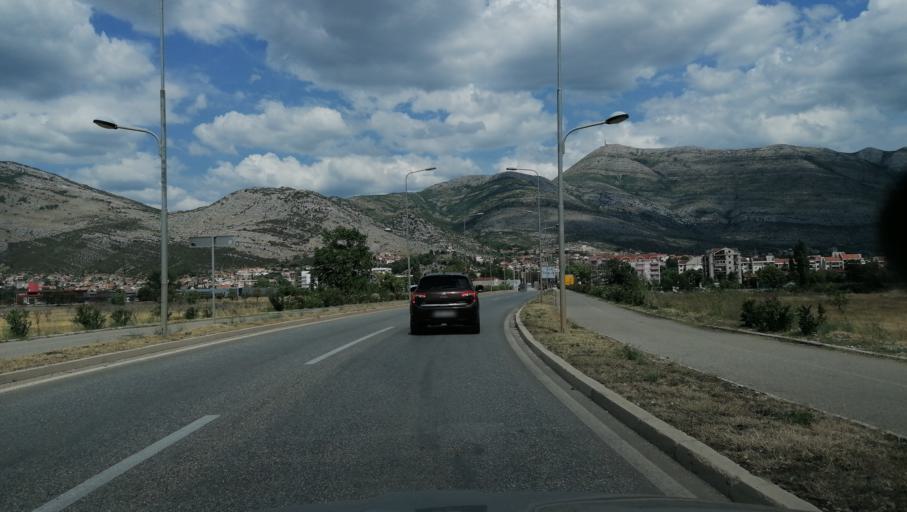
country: BA
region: Republika Srpska
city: Trebinje
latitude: 42.7020
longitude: 18.3434
